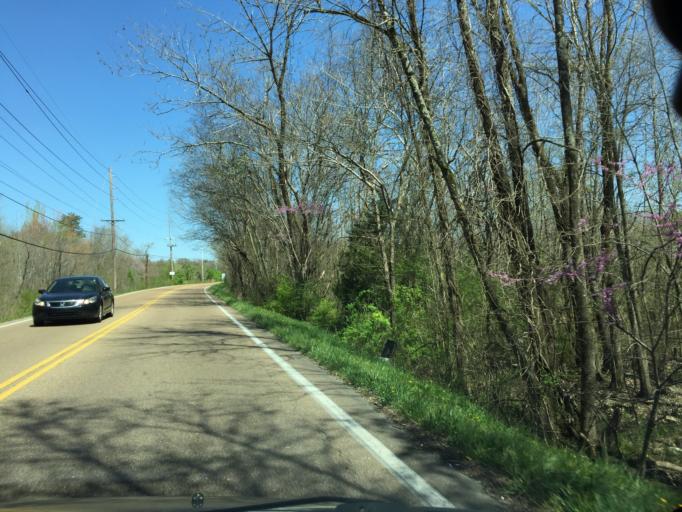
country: US
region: Tennessee
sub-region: Hamilton County
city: Middle Valley
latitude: 35.1649
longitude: -85.2105
